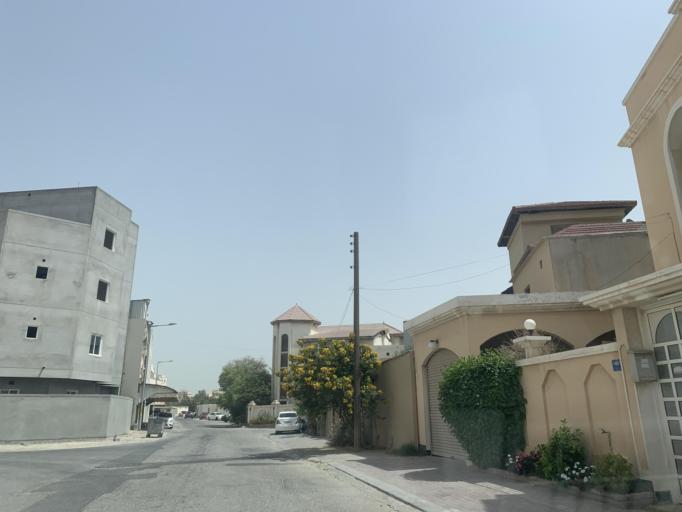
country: BH
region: Northern
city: Madinat `Isa
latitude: 26.1797
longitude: 50.5556
